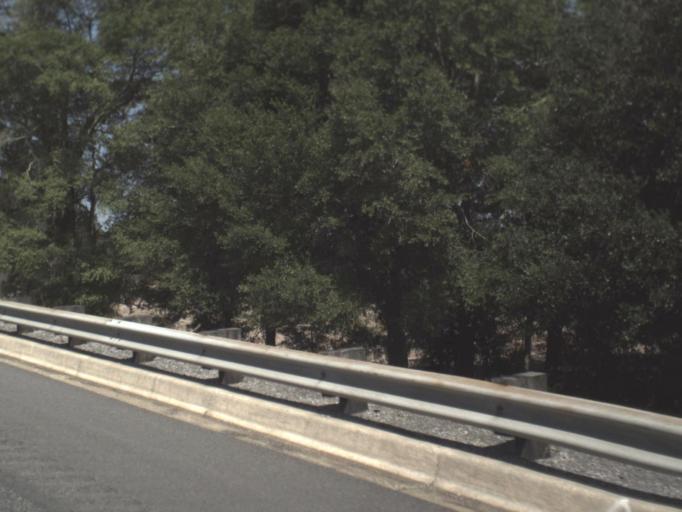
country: US
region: Florida
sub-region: Suwannee County
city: Live Oak
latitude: 30.3449
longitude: -83.0880
